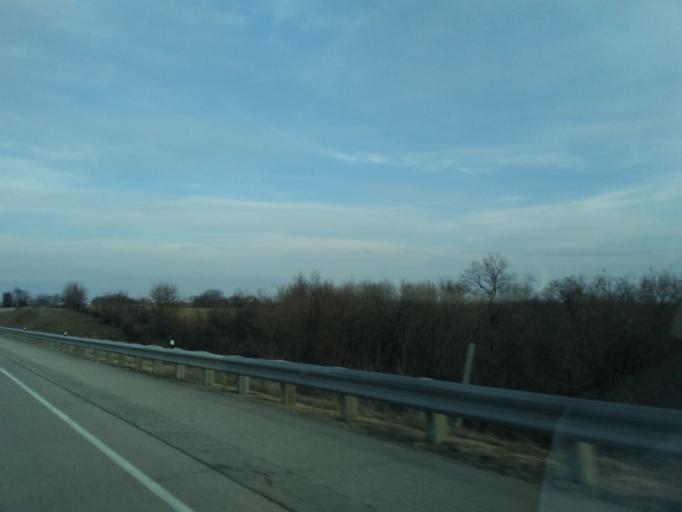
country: US
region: Wisconsin
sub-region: Dane County
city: Mount Horeb
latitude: 43.0102
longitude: -89.8004
